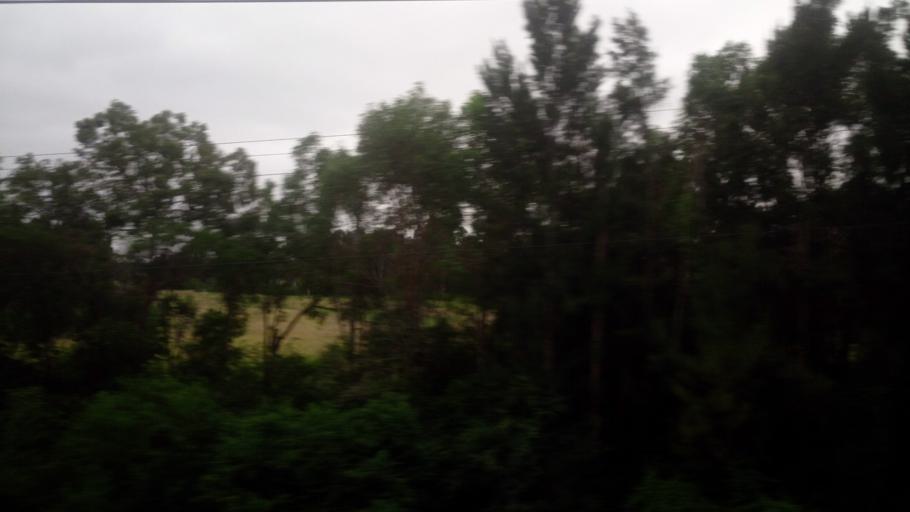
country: AU
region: New South Wales
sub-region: Blacktown
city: Mount Druitt
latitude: -33.7658
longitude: 150.7979
